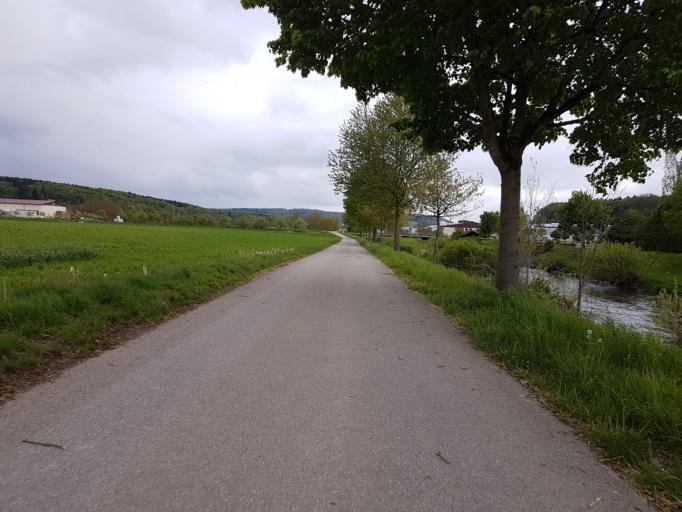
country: DE
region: Baden-Wuerttemberg
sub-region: Freiburg Region
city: Wutoschingen
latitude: 47.6478
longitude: 8.3540
